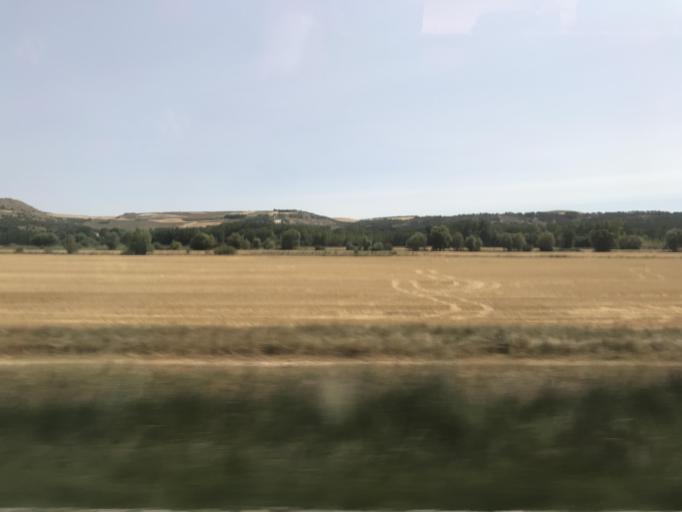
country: ES
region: Castille and Leon
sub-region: Provincia de Burgos
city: Pampliega
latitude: 42.2247
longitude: -3.9896
